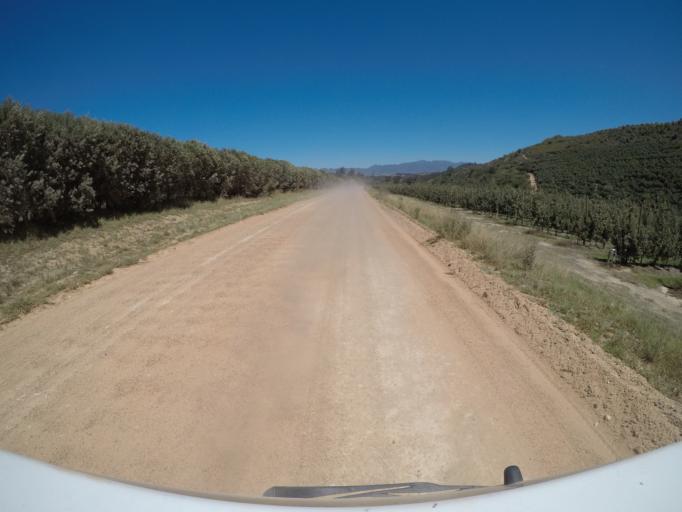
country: ZA
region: Western Cape
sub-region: Overberg District Municipality
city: Grabouw
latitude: -34.2447
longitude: 19.1057
